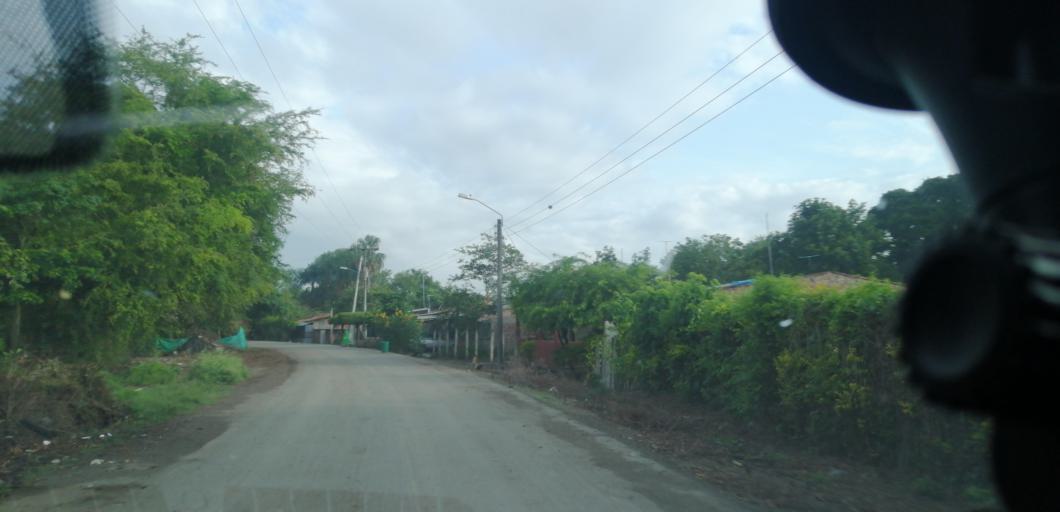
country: CO
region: Valle del Cauca
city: Palmira
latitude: 3.5387
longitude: -76.3593
